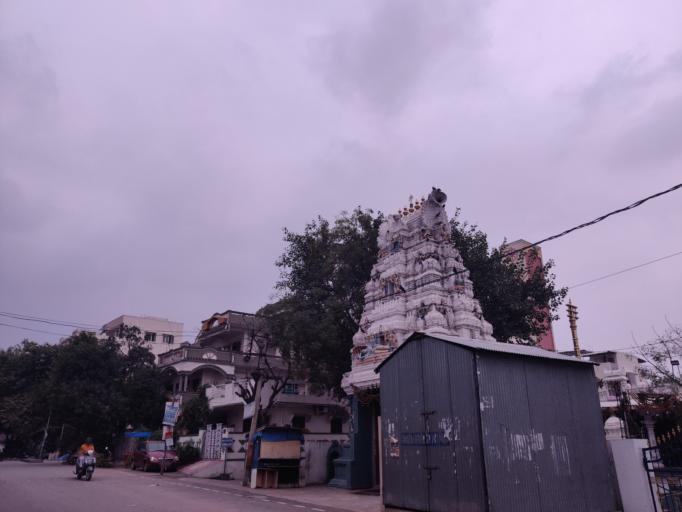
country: IN
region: Telangana
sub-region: Hyderabad
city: Hyderabad
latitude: 17.4077
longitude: 78.3946
